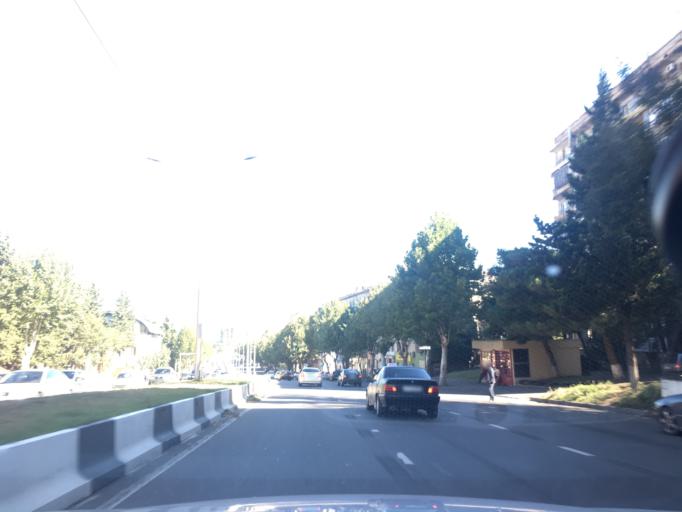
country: GE
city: Zahesi
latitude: 41.7733
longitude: 44.7943
